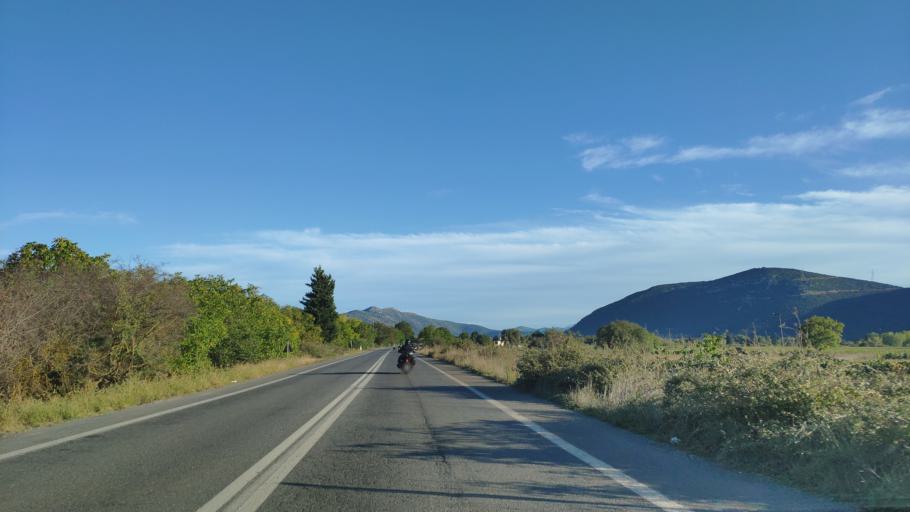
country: GR
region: Peloponnese
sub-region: Nomos Arkadias
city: Tripoli
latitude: 37.5966
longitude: 22.3741
